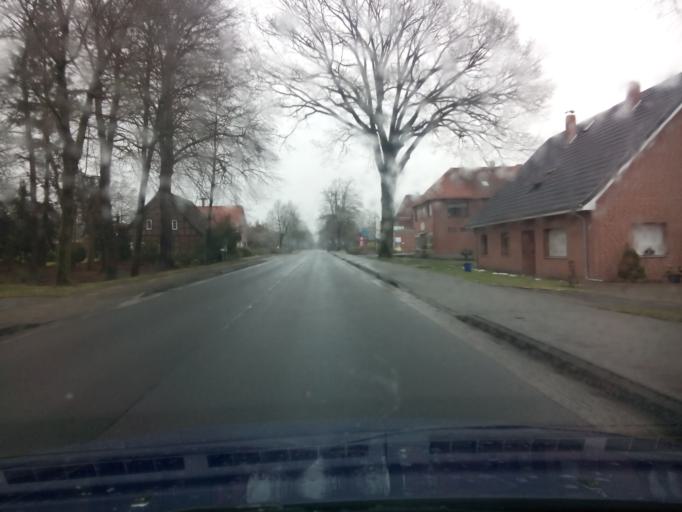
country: DE
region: Lower Saxony
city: Basdahl
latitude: 53.4460
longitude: 9.0015
